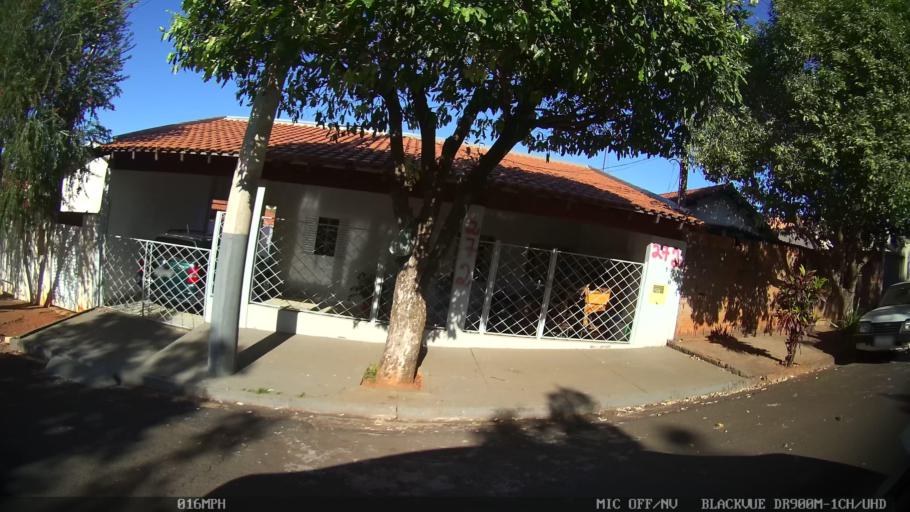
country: BR
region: Sao Paulo
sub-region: Olimpia
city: Olimpia
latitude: -20.7418
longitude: -48.8859
